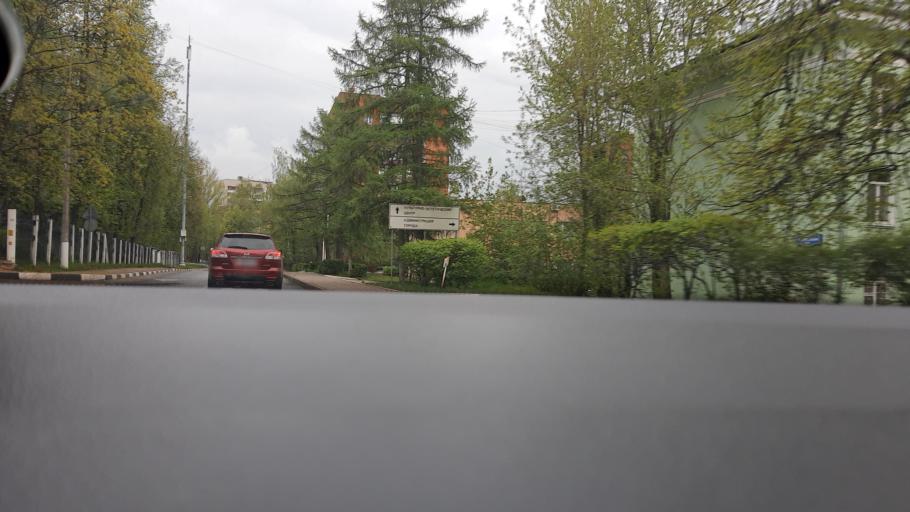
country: RU
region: Moskovskaya
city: Dzerzhinskiy
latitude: 55.6261
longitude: 37.8496
